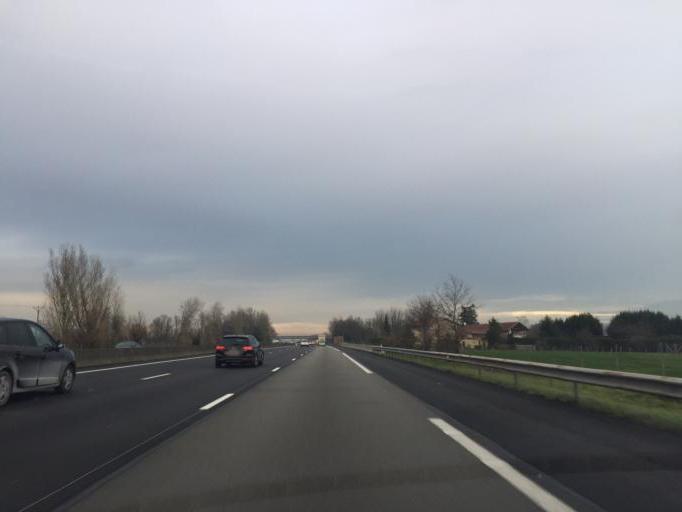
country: FR
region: Rhone-Alpes
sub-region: Departement du Rhone
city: Saint-Georges-de-Reneins
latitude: 46.0682
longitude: 4.7402
